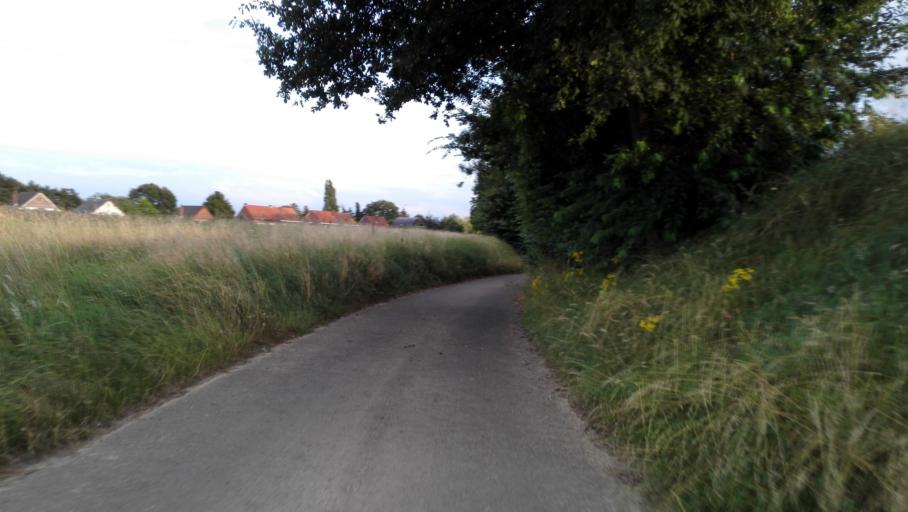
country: BE
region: Flanders
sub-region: Provincie Vlaams-Brabant
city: Bierbeek
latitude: 50.8359
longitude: 4.7454
